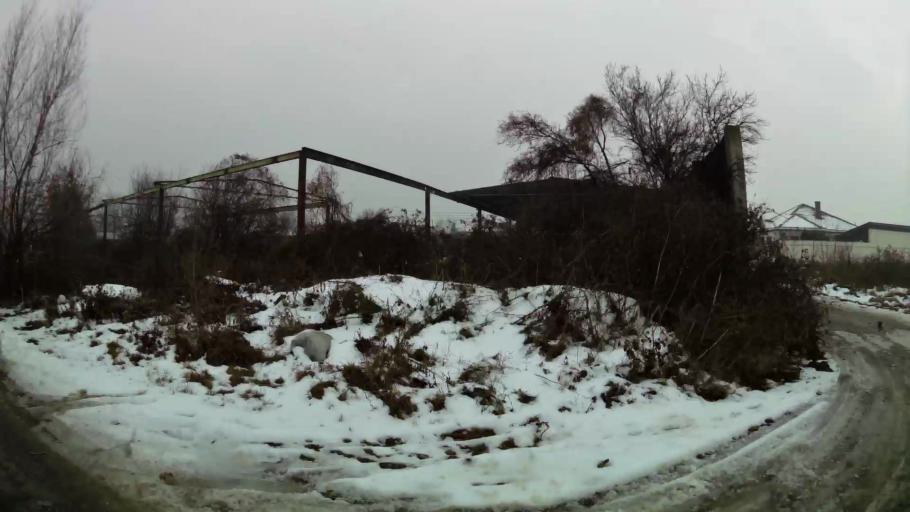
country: MK
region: Petrovec
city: Petrovec
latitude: 41.9346
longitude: 21.6151
